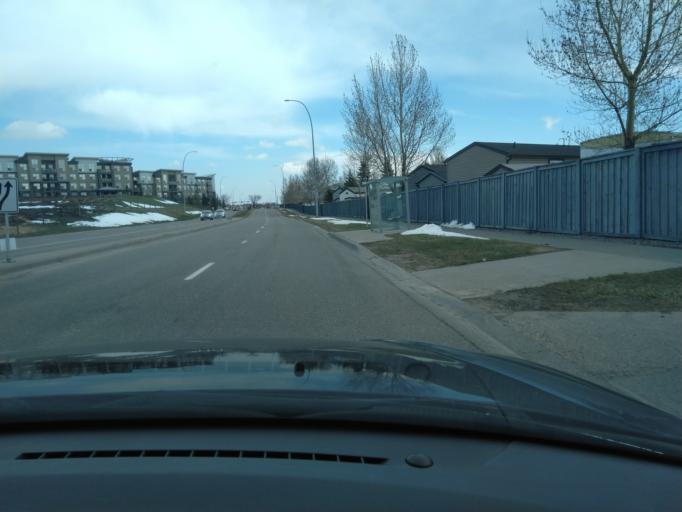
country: CA
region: Alberta
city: Calgary
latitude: 51.1284
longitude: -114.2138
